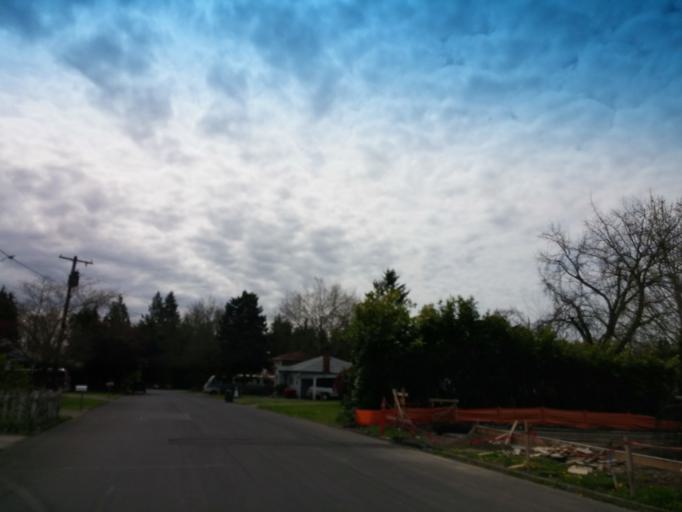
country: US
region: Oregon
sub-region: Washington County
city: Cedar Mill
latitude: 45.5251
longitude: -122.8126
